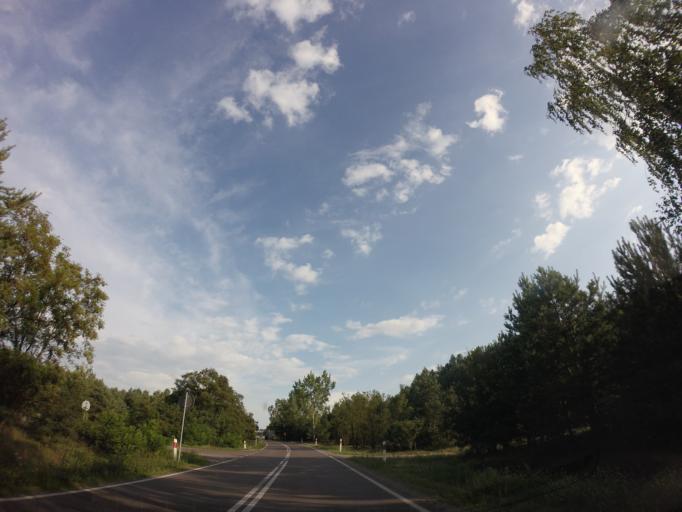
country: PL
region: Lublin Voivodeship
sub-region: Powiat lubartowski
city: Jeziorzany
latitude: 51.5692
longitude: 22.2934
